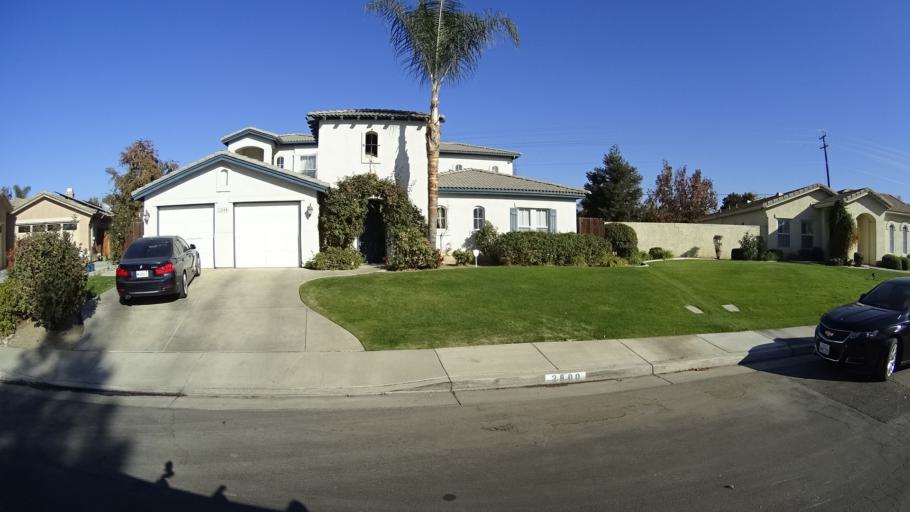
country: US
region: California
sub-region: Kern County
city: Rosedale
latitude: 35.3294
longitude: -119.1287
